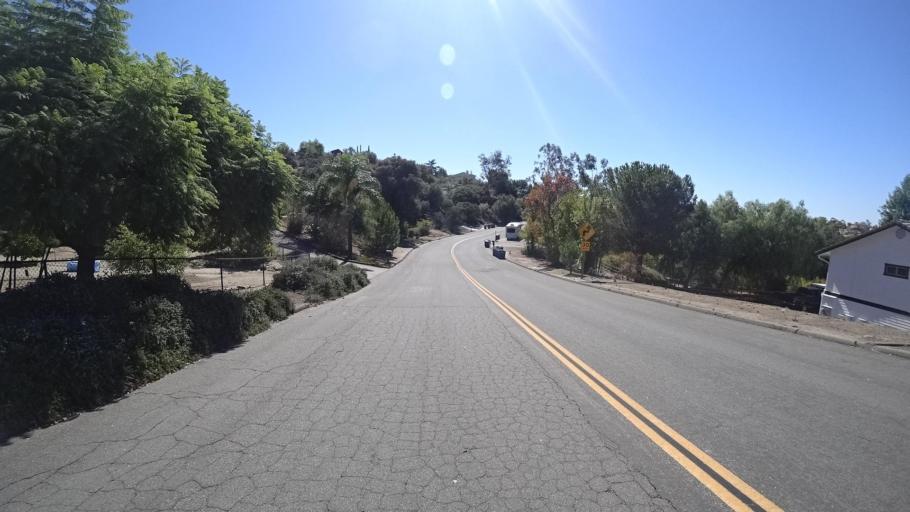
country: US
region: California
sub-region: San Diego County
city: Alpine
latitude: 32.8515
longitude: -116.7630
